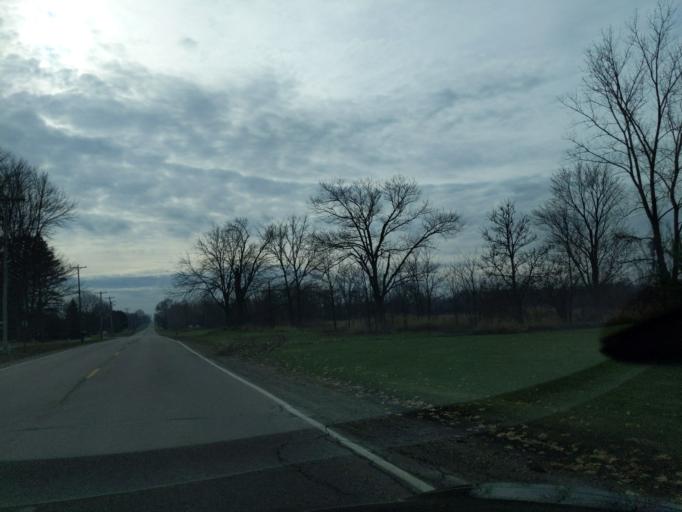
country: US
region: Michigan
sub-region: Ingham County
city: Holt
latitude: 42.6283
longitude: -84.5232
